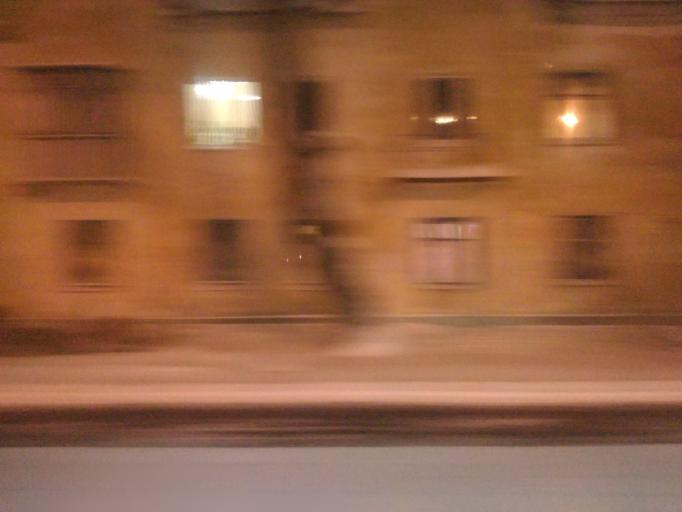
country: RU
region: Ulyanovsk
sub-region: Ulyanovskiy Rayon
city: Ulyanovsk
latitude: 54.3248
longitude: 48.3801
